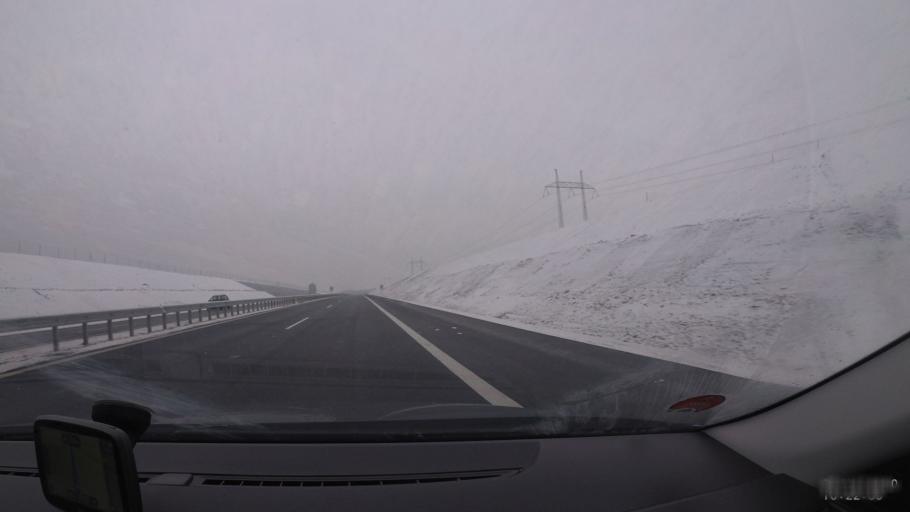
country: CZ
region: Central Bohemia
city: Revnicov
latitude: 50.1775
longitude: 13.8003
